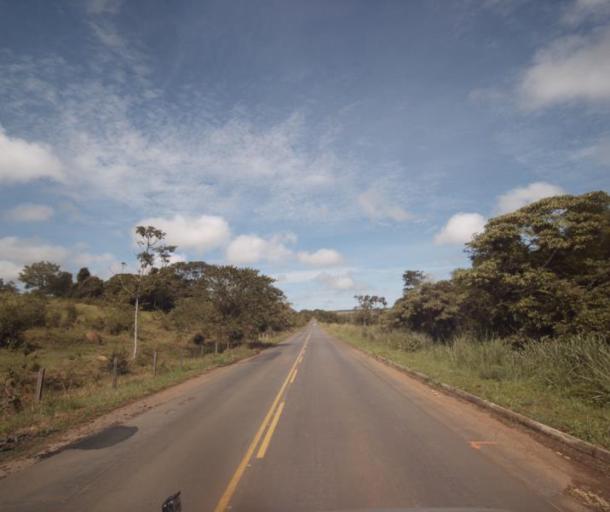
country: BR
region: Goias
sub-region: Pirenopolis
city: Pirenopolis
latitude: -15.9877
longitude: -48.8314
